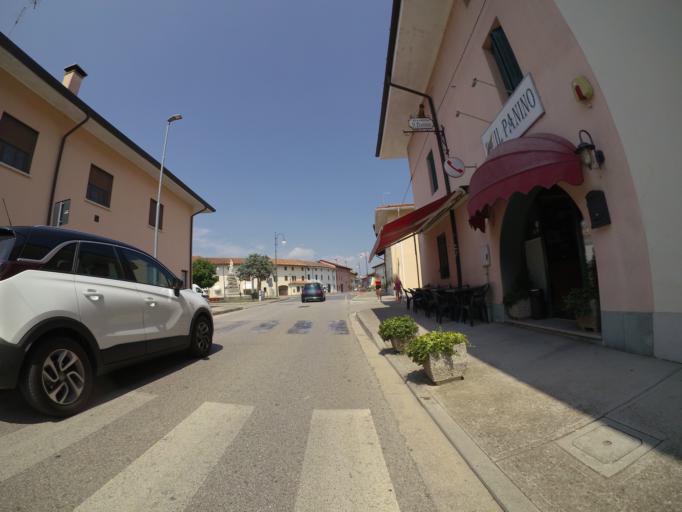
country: IT
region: Friuli Venezia Giulia
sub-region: Provincia di Udine
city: Sedegliano
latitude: 46.0011
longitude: 12.9648
